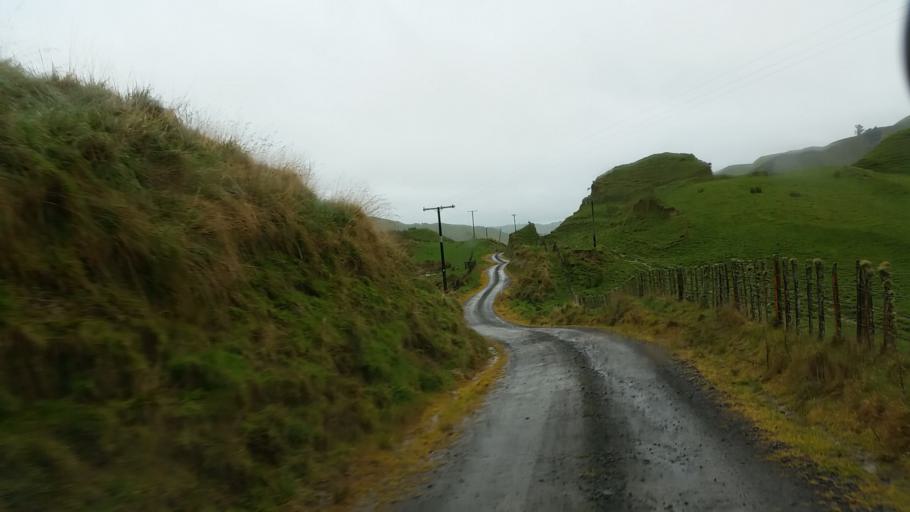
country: NZ
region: Taranaki
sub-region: South Taranaki District
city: Eltham
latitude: -39.4756
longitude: 174.4137
